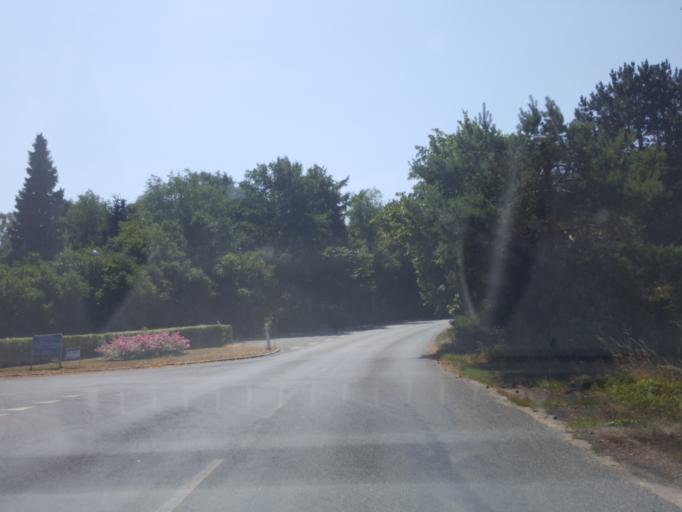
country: DK
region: Capital Region
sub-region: Fredensborg Kommune
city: Kokkedal
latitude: 55.9295
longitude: 12.4681
